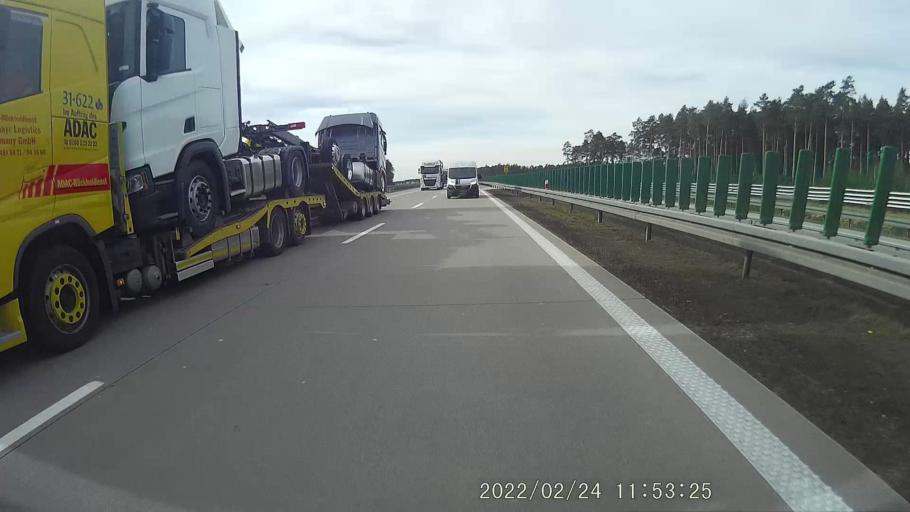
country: PL
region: Lower Silesian Voivodeship
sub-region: Powiat polkowicki
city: Radwanice
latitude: 51.6298
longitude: 15.9765
